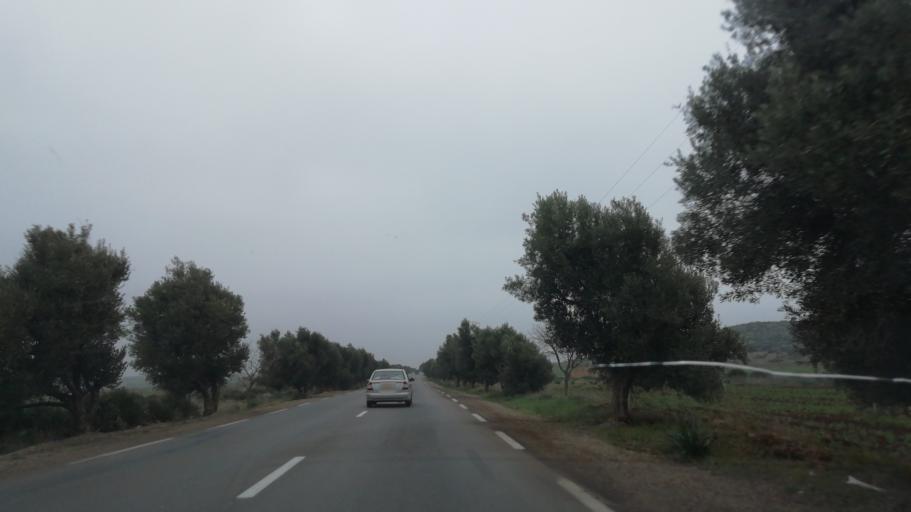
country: DZ
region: Mascara
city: Mascara
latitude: 35.3107
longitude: 0.3975
